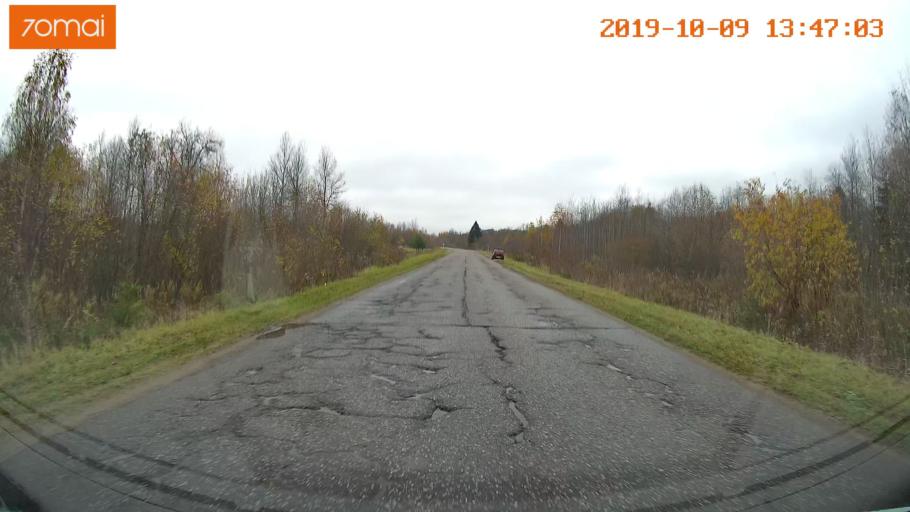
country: RU
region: Kostroma
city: Buy
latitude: 58.3888
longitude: 41.2223
